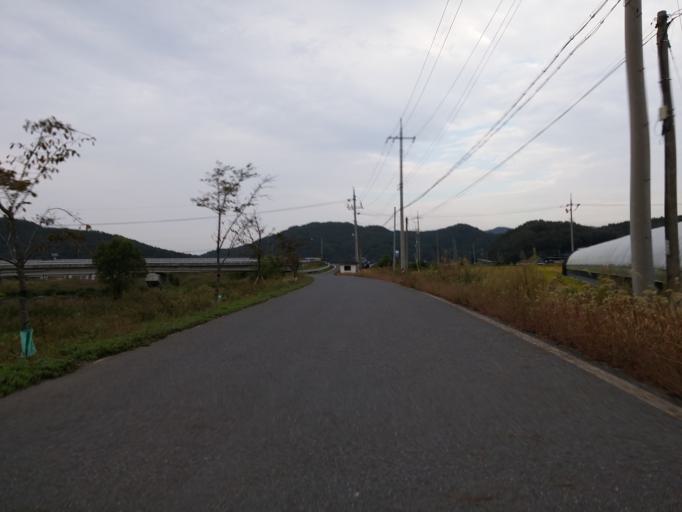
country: KR
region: Daejeon
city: Daejeon
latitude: 36.2465
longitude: 127.3156
